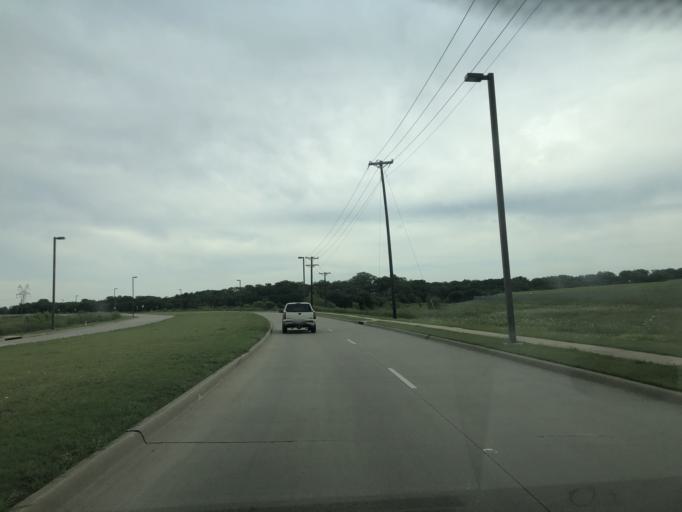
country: US
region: Texas
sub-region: Dallas County
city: Grand Prairie
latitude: 32.7777
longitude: -96.9819
